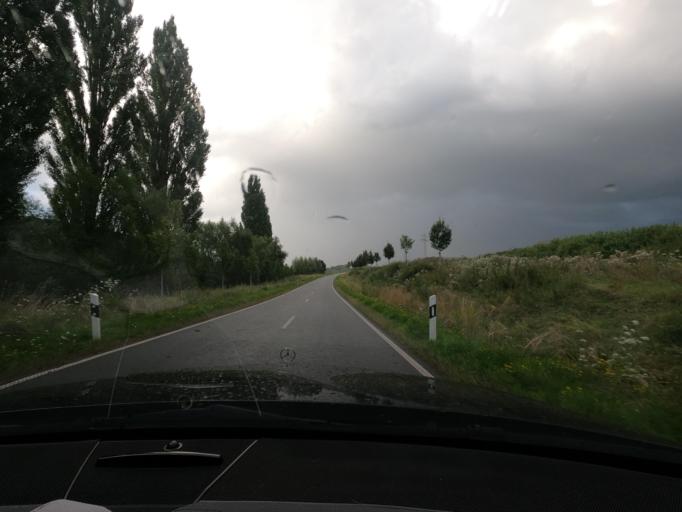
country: DE
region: Hesse
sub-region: Regierungsbezirk Kassel
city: Wolfhagen
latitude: 51.3218
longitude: 9.1962
